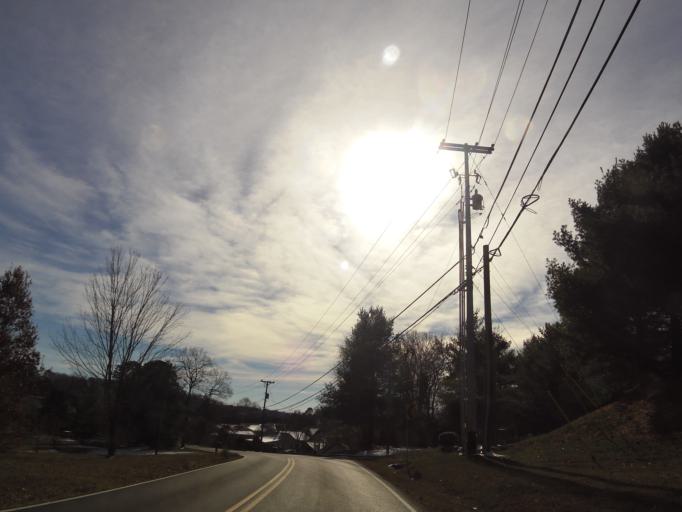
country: US
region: Tennessee
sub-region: Blount County
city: Louisville
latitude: 35.9082
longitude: -84.0522
